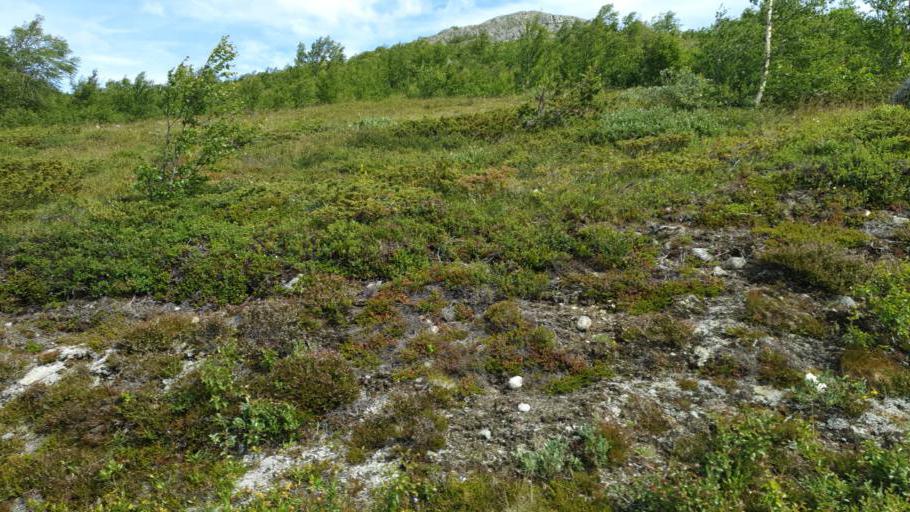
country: NO
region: Oppland
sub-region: Lom
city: Fossbergom
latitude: 61.4945
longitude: 8.8128
